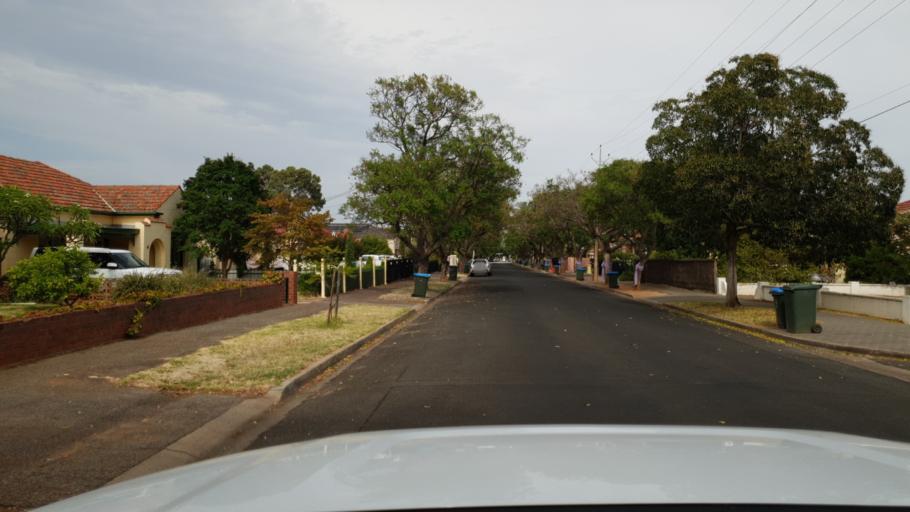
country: AU
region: South Australia
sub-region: Mitcham
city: Clarence Gardens
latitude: -34.9746
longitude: 138.5854
